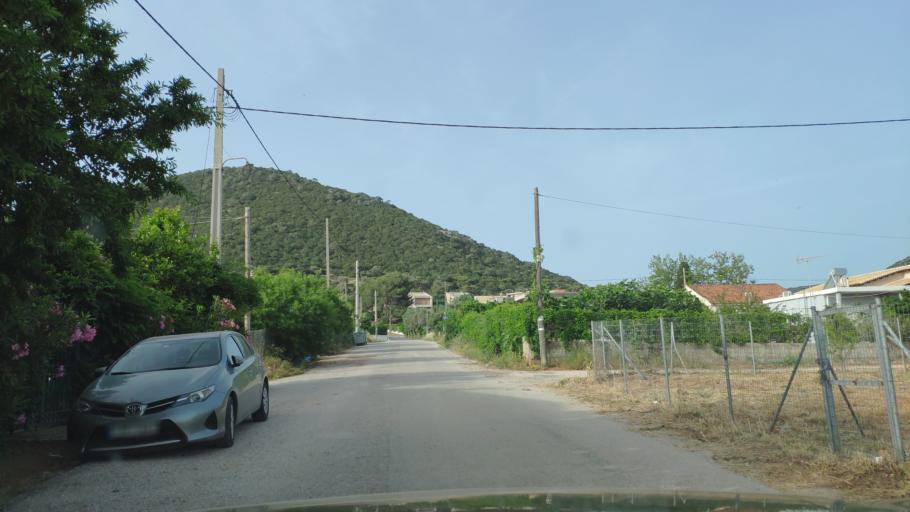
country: GR
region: Attica
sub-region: Nomarchia Anatolikis Attikis
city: Limin Mesoyaias
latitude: 37.8629
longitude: 24.0294
